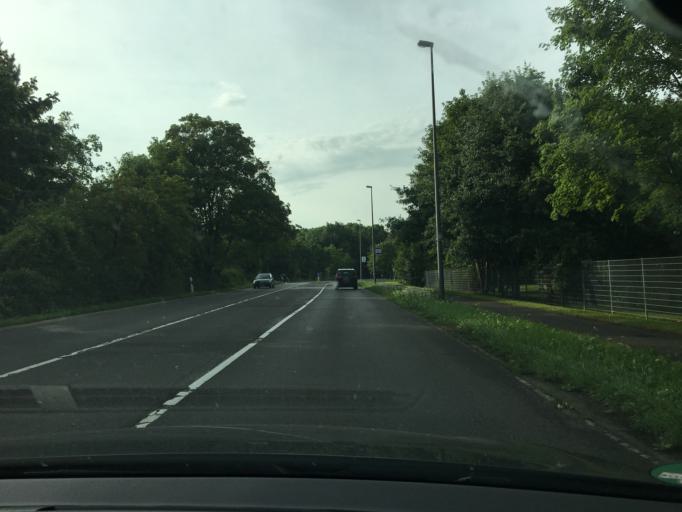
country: DE
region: North Rhine-Westphalia
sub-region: Regierungsbezirk Koln
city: Poll
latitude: 50.8751
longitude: 6.9968
